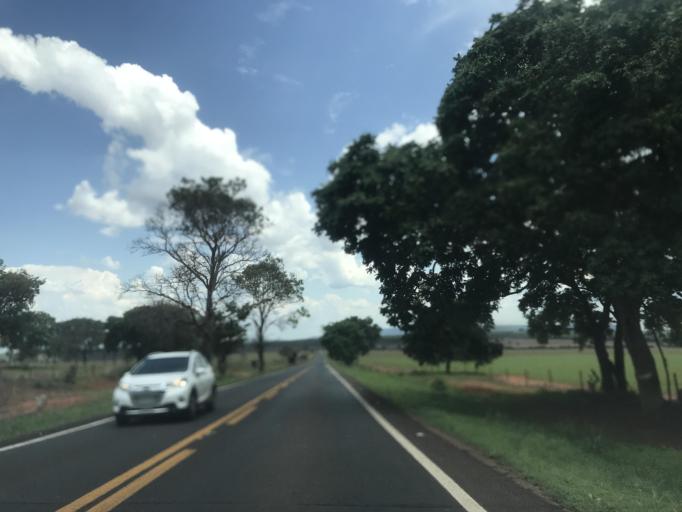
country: BR
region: Goias
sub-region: Caldas Novas
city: Caldas Novas
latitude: -17.6273
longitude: -48.7065
